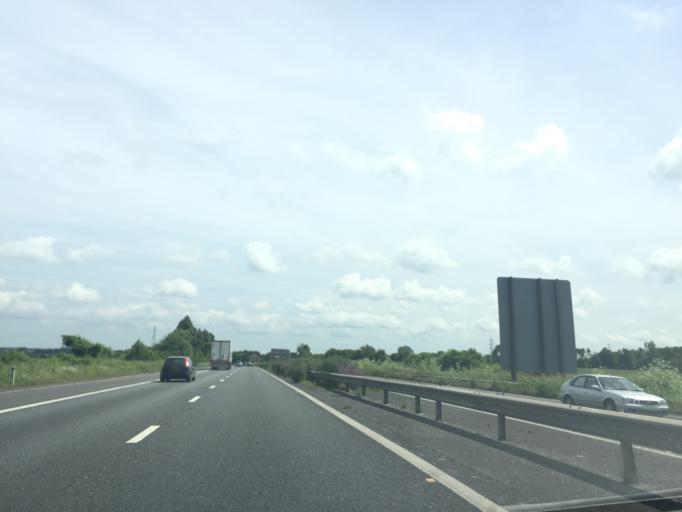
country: GB
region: England
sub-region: Kent
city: Newington
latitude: 51.3233
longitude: 0.6801
